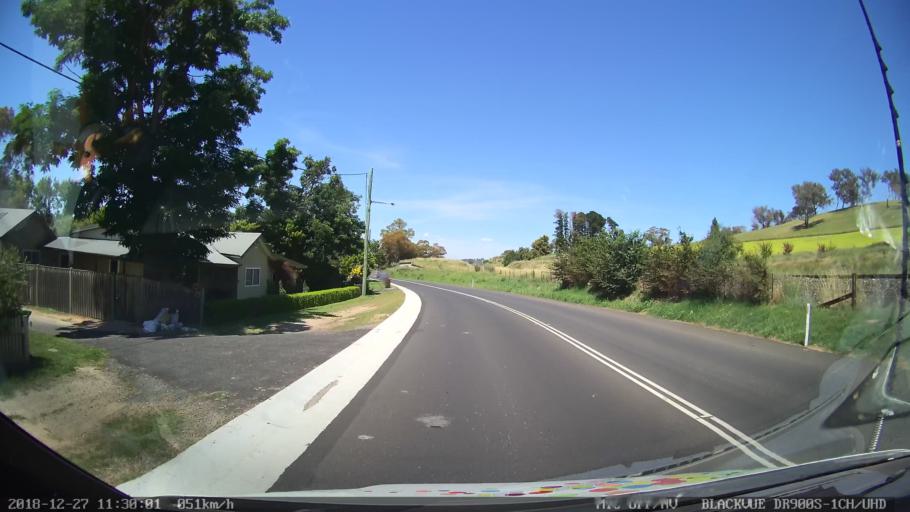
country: AU
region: New South Wales
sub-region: Bathurst Regional
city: Perthville
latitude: -33.4847
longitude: 149.5480
